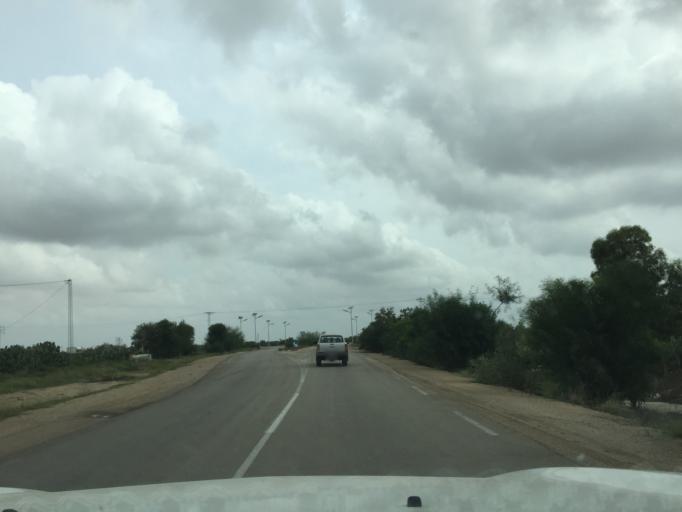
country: TN
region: Al Munastir
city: Sidi Bin Nur
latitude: 35.5429
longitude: 10.8632
